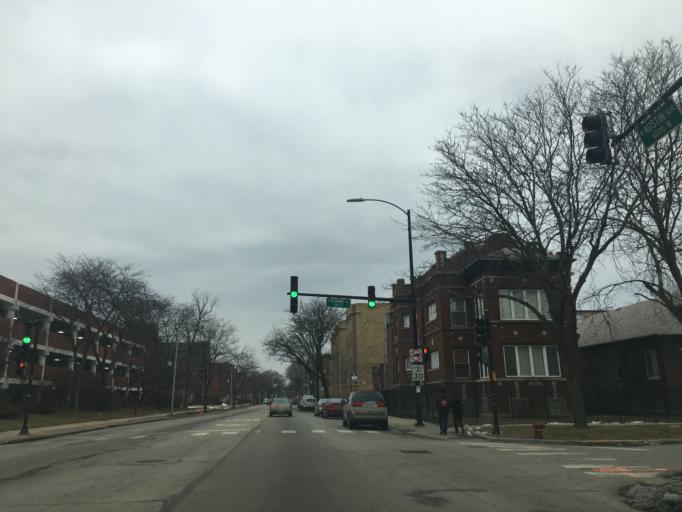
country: US
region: Illinois
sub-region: Cook County
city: Oak Park
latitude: 41.8917
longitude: -87.7750
